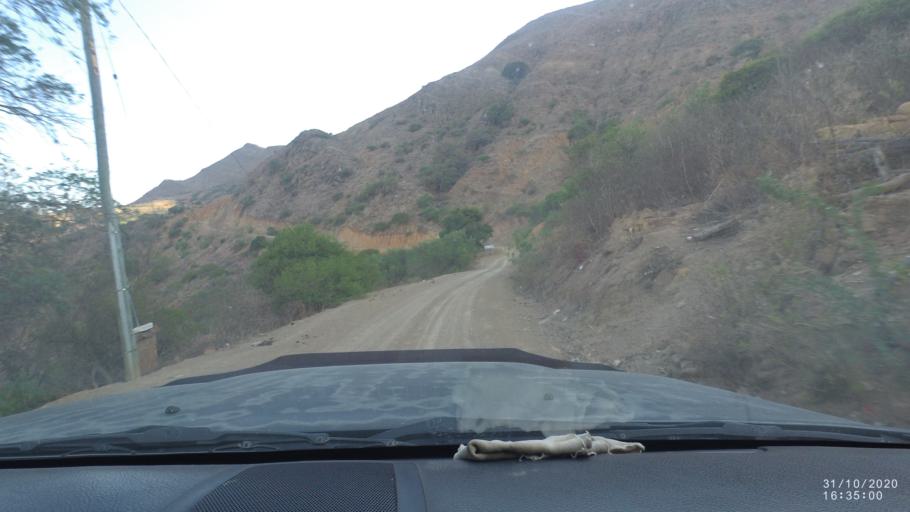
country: BO
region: Chuquisaca
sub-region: Provincia Zudanez
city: Mojocoya
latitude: -18.4509
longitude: -64.5832
